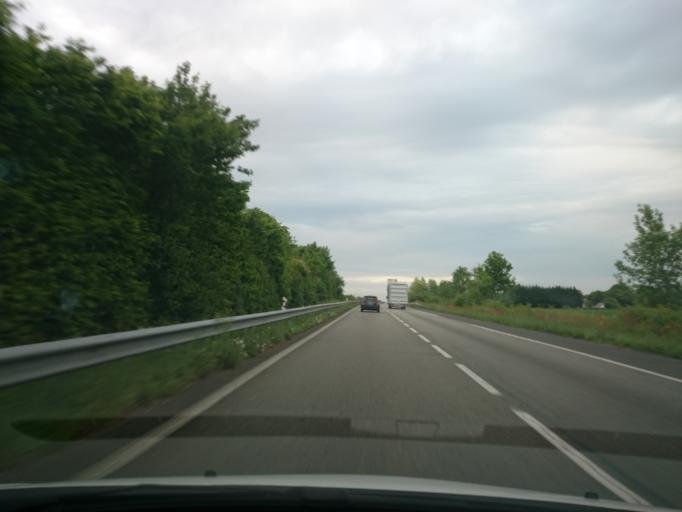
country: FR
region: Pays de la Loire
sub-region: Departement de la Loire-Atlantique
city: Heric
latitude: 47.3965
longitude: -1.6445
